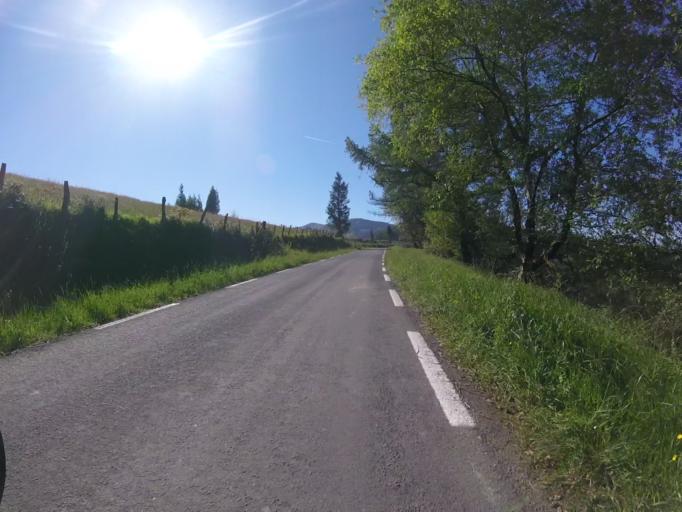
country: ES
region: Basque Country
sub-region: Provincia de Guipuzcoa
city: Errezil
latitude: 43.2073
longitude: -2.1993
